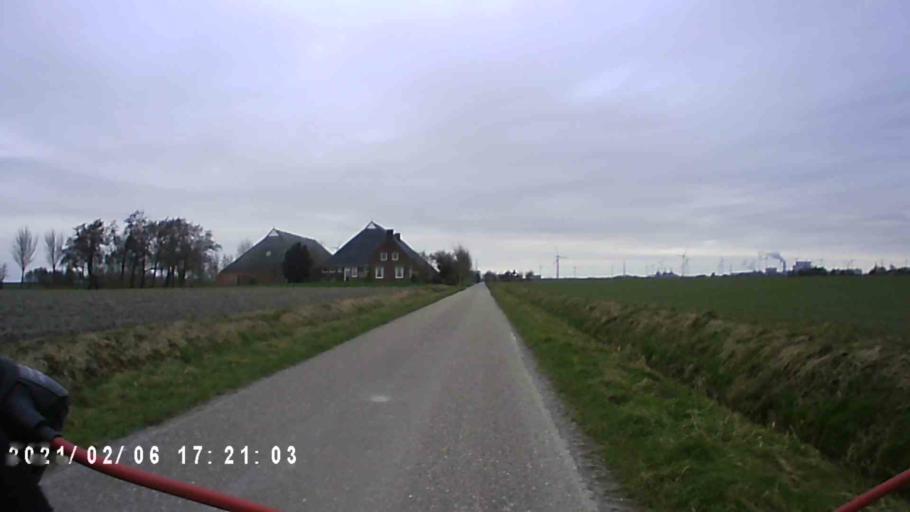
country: NL
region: Groningen
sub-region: Gemeente Appingedam
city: Appingedam
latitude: 53.4310
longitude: 6.7945
